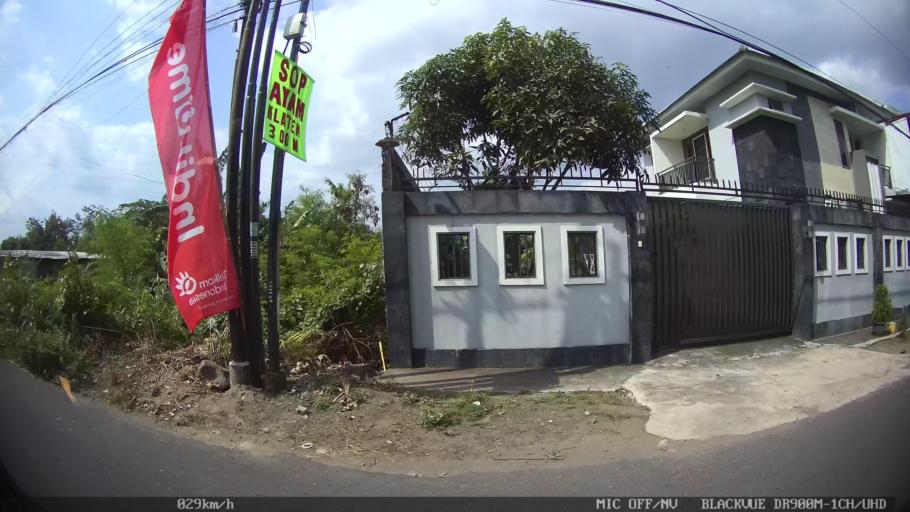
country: ID
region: Daerah Istimewa Yogyakarta
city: Yogyakarta
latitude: -7.7592
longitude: 110.3437
